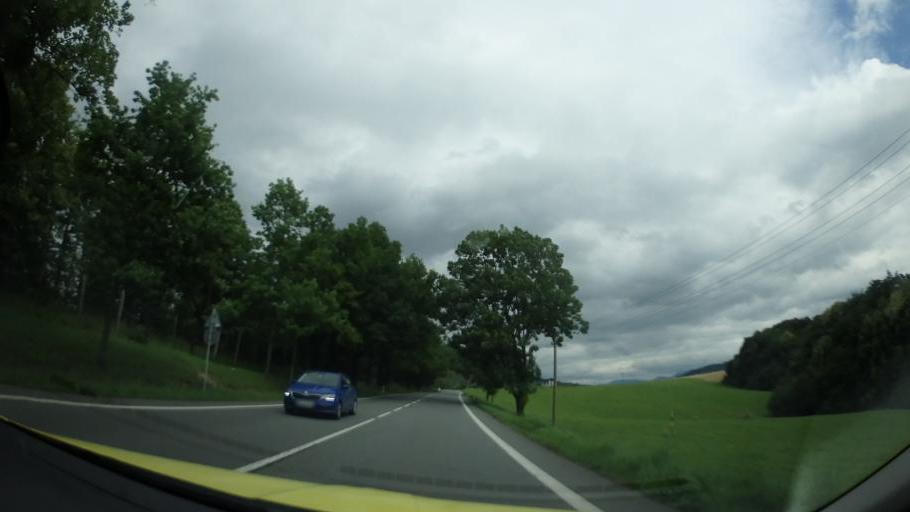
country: CZ
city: Stramberk
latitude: 49.5753
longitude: 18.1144
